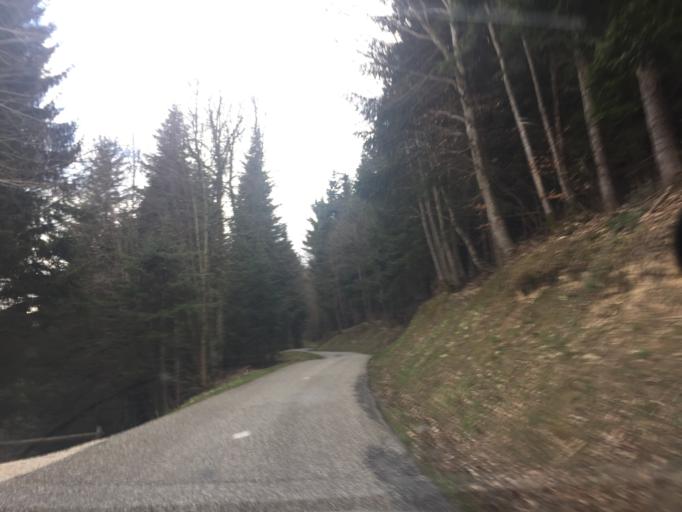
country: FR
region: Rhone-Alpes
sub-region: Departement de la Savoie
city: La Motte-Servolex
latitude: 45.5850
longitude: 5.8277
